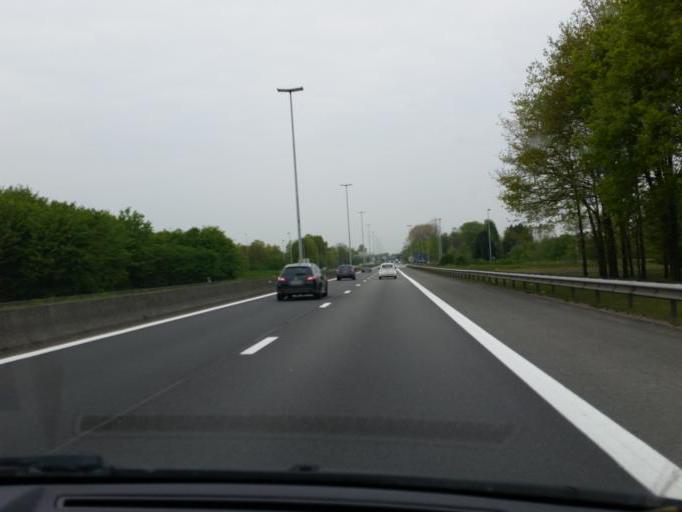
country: BE
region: Flanders
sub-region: Provincie Oost-Vlaanderen
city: Destelbergen
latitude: 51.0522
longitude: 3.8186
